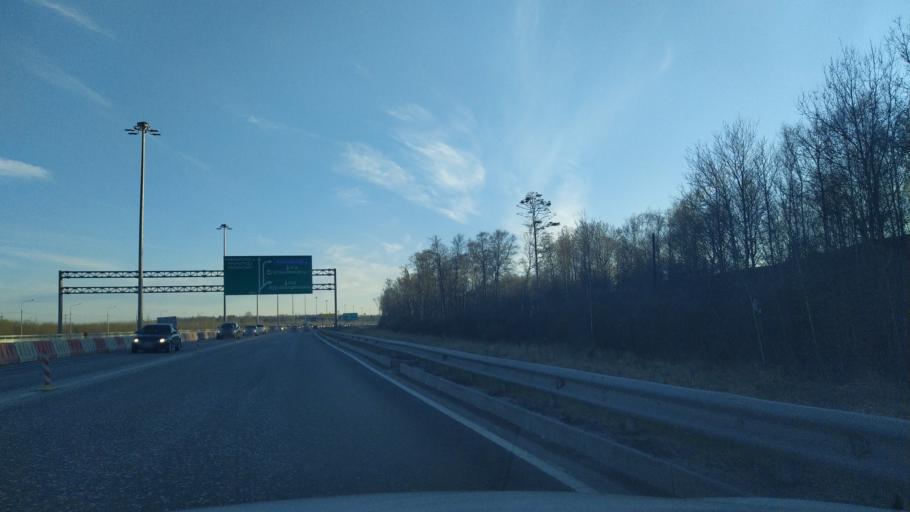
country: RU
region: St.-Petersburg
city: Levashovo
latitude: 60.0704
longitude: 30.1743
